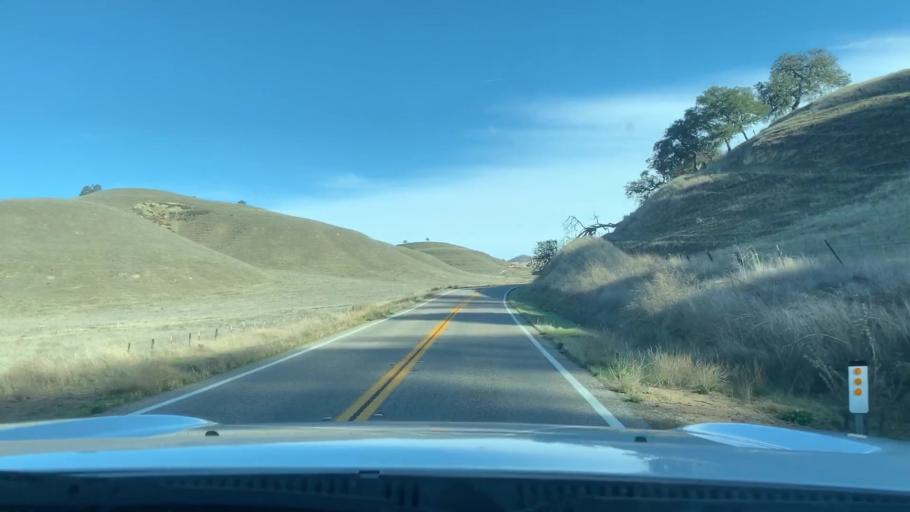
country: US
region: California
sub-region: Monterey County
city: King City
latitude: 36.1844
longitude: -120.8458
